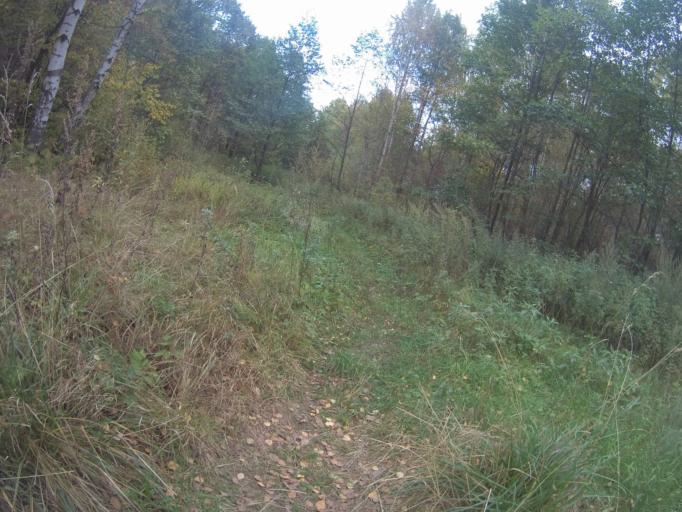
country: RU
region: Vladimir
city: Raduzhnyy
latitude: 55.9892
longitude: 40.3726
